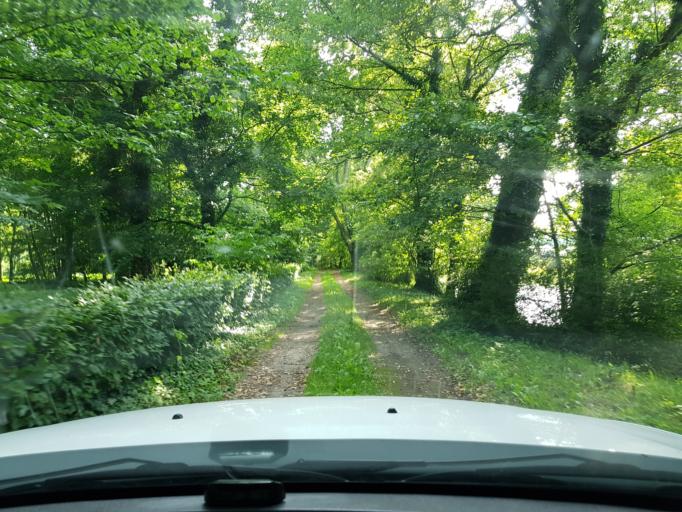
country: PL
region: West Pomeranian Voivodeship
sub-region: Powiat gryfinski
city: Chojna
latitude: 52.9976
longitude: 14.4840
